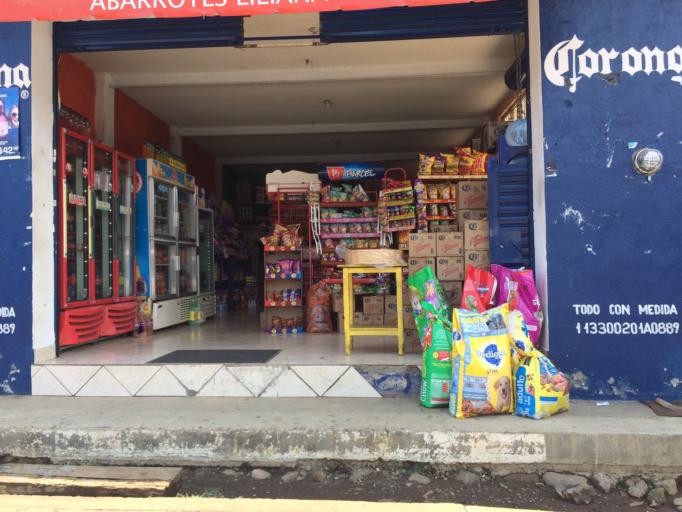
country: MX
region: Michoacan
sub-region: Periban
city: San Francisco Periban
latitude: 19.5552
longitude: -102.3999
